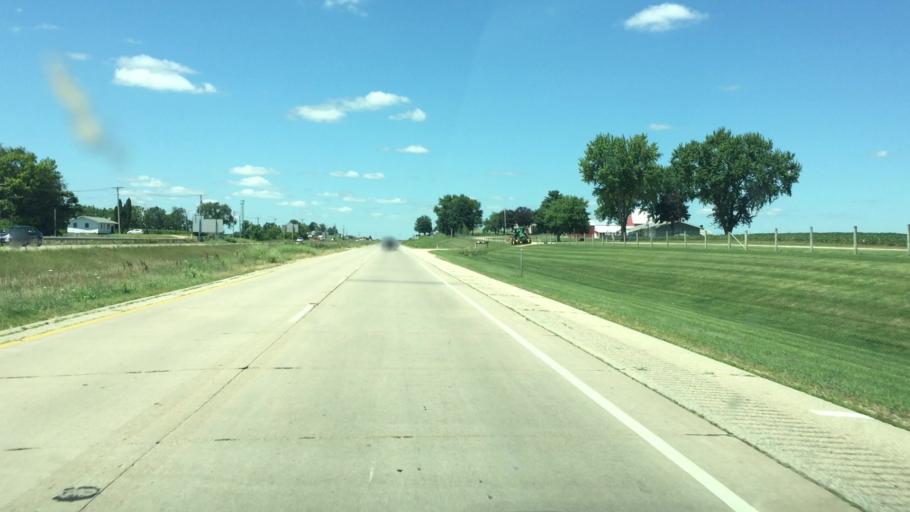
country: US
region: Wisconsin
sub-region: Grant County
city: Dickeyville
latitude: 42.5610
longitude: -90.6104
